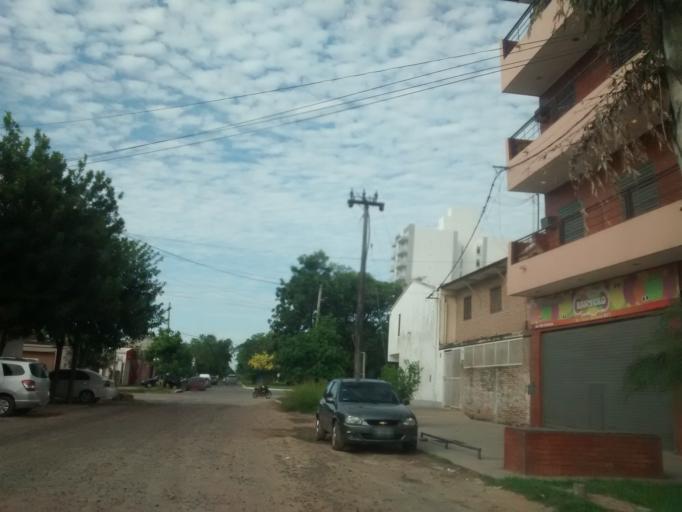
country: AR
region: Chaco
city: Resistencia
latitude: -27.4508
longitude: -58.9718
